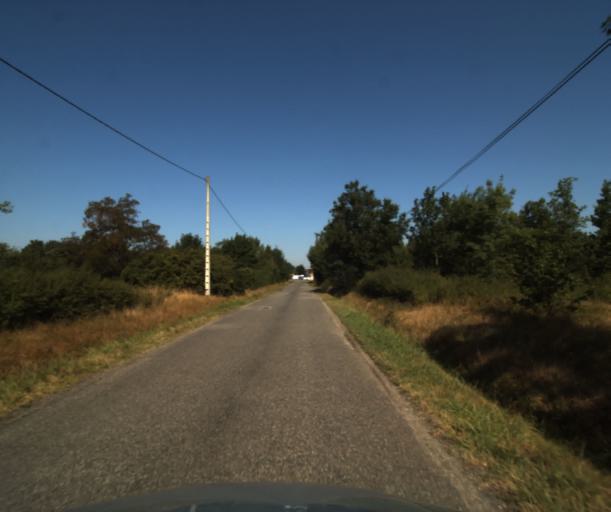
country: FR
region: Midi-Pyrenees
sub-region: Departement de la Haute-Garonne
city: Labastidette
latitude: 43.4582
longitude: 1.2536
